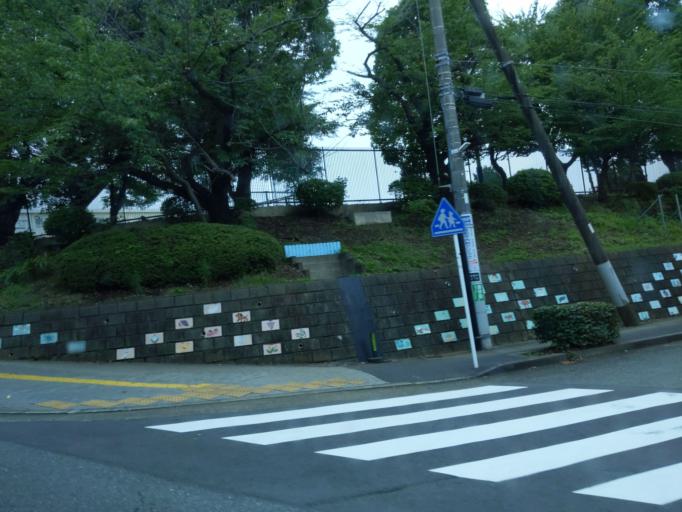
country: JP
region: Tokyo
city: Chofugaoka
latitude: 35.5873
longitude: 139.5796
